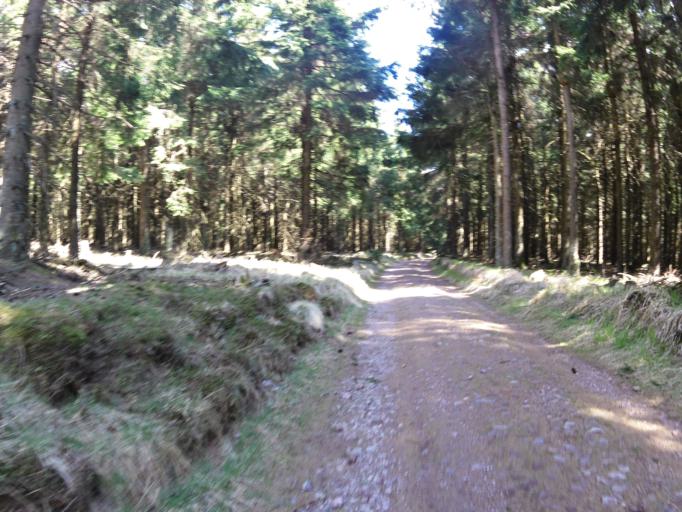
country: DE
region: Thuringia
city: Unterschonau
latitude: 50.7378
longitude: 10.5818
